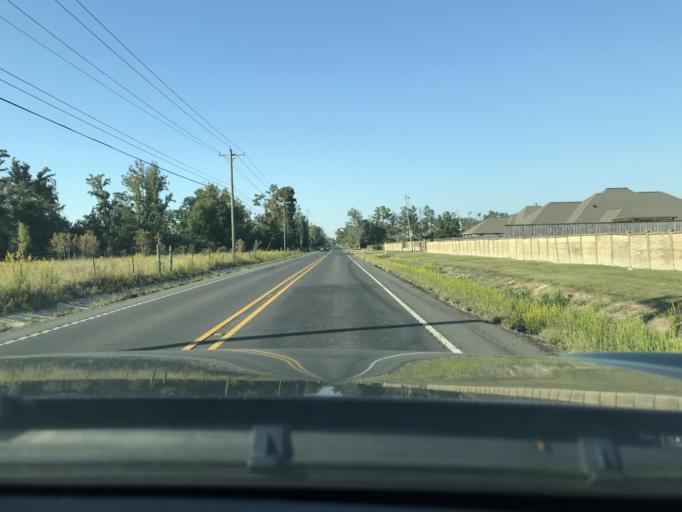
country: US
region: Louisiana
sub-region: Calcasieu Parish
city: Moss Bluff
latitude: 30.3103
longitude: -93.2583
